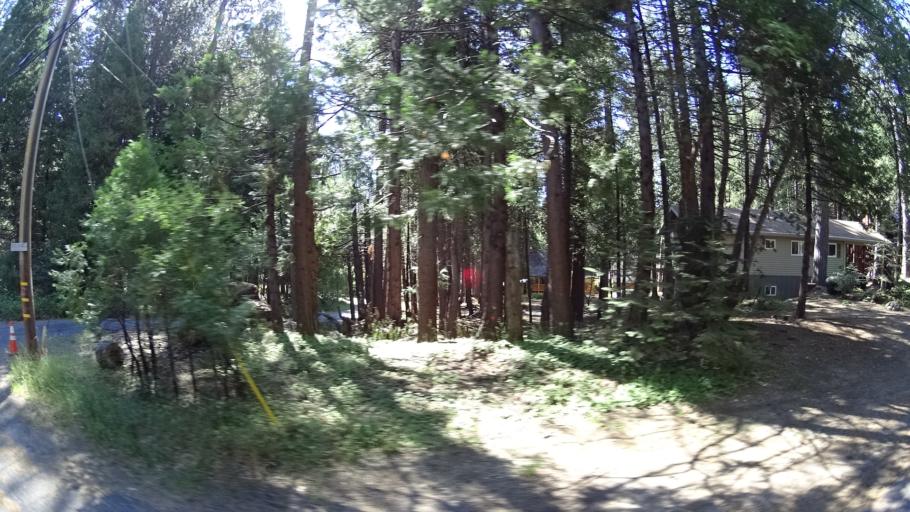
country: US
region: California
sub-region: Calaveras County
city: Arnold
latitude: 38.2903
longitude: -120.2741
